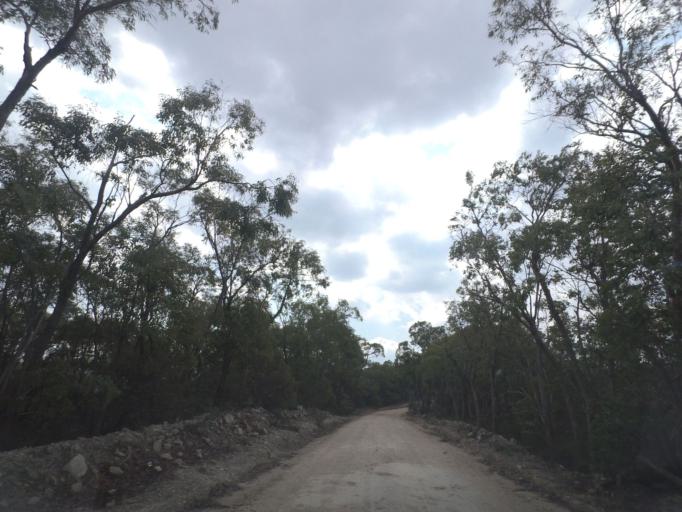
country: AU
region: Victoria
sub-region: Moorabool
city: Bacchus Marsh
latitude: -37.5536
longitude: 144.4216
